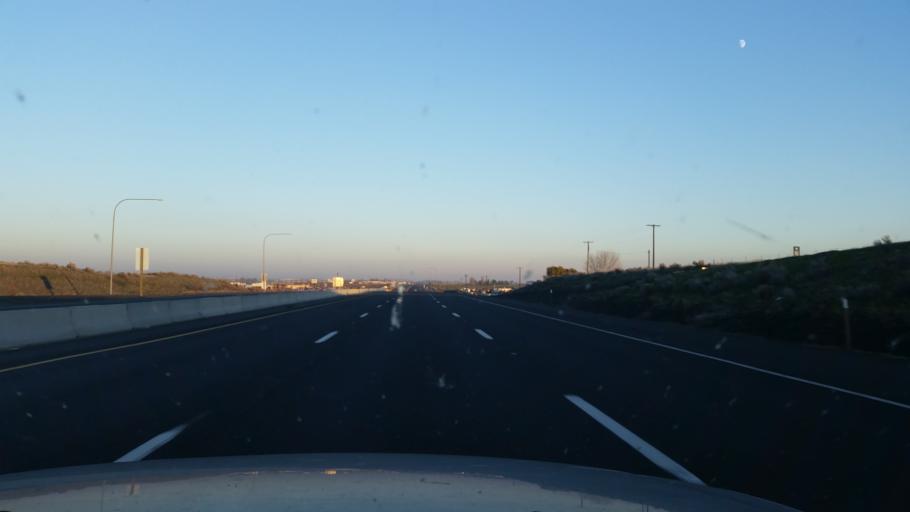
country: US
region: Washington
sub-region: Grant County
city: Moses Lake
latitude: 47.0989
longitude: -119.2425
